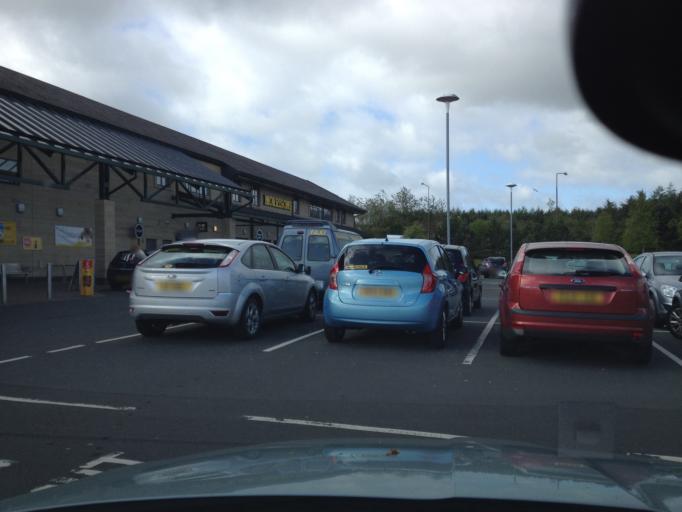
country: GB
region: Scotland
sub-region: West Lothian
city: Livingston
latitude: 55.8769
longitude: -3.5269
